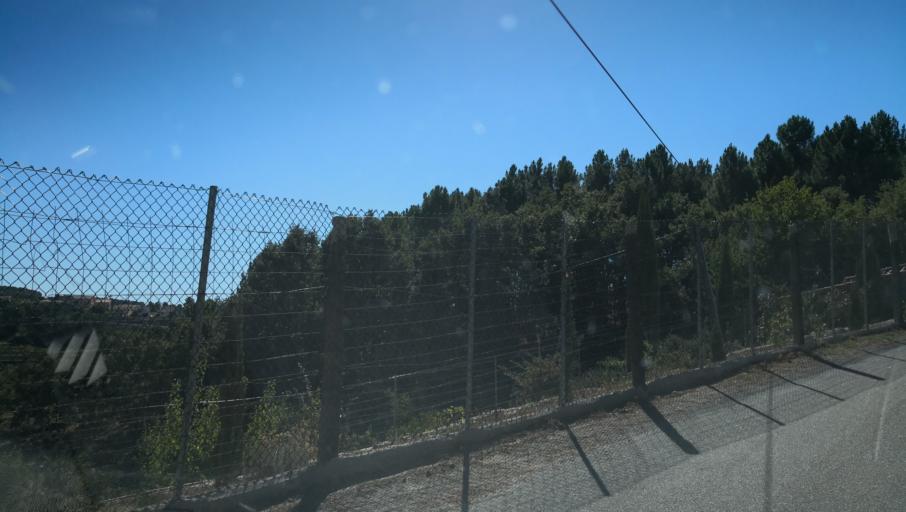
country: PT
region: Vila Real
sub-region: Vila Real
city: Vila Real
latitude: 41.3199
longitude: -7.7244
